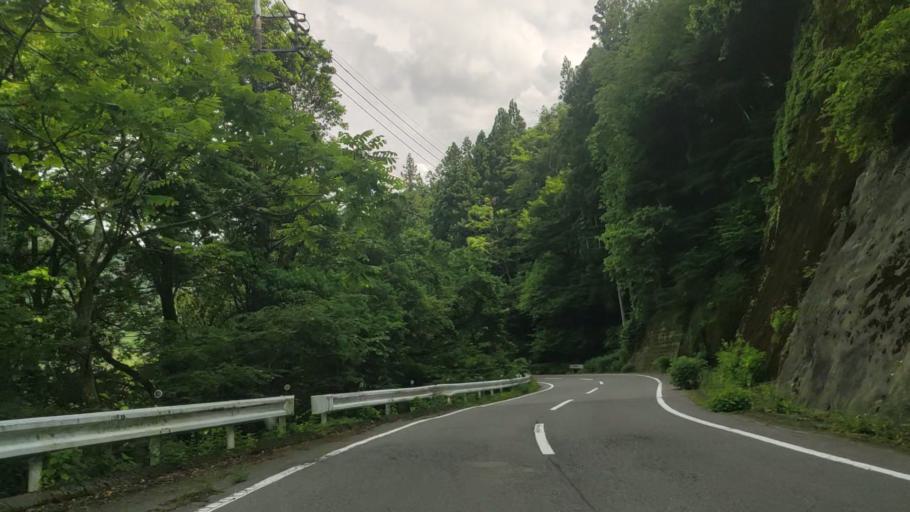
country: JP
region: Gunma
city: Tomioka
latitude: 36.1497
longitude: 138.7320
